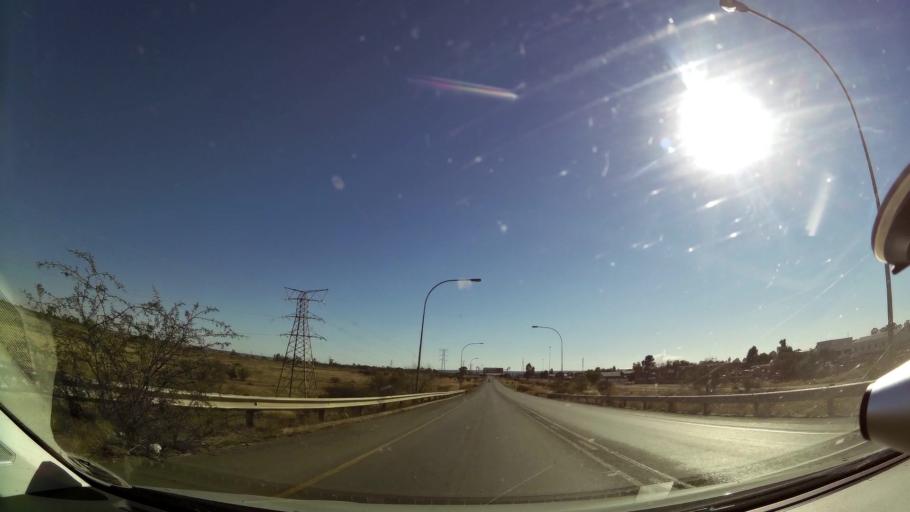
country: ZA
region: Northern Cape
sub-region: Frances Baard District Municipality
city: Kimberley
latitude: -28.7114
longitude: 24.7762
